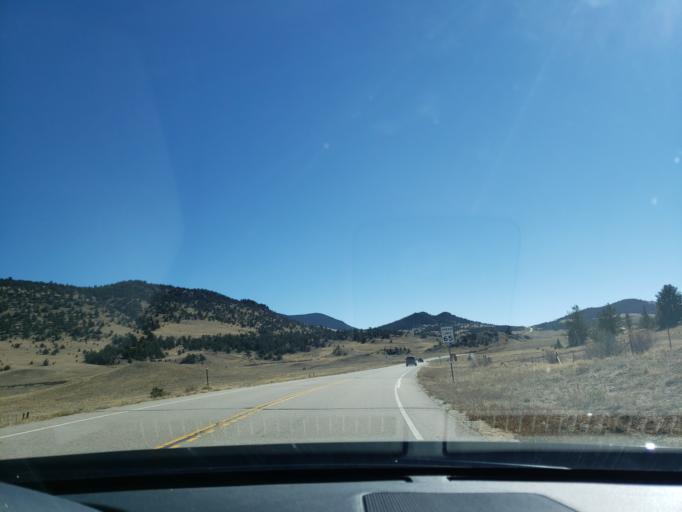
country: US
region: Colorado
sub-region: Chaffee County
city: Salida
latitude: 38.8619
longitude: -105.6583
